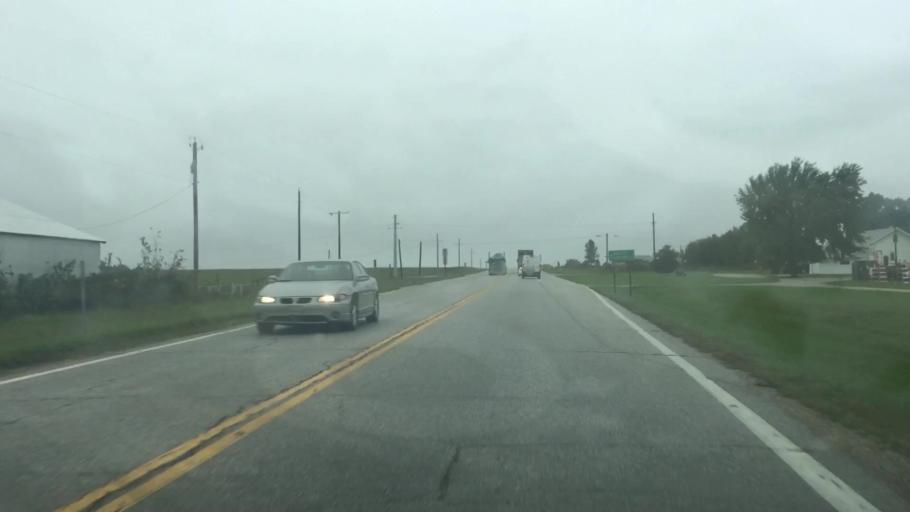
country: US
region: Kansas
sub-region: Anderson County
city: Garnett
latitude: 38.2284
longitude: -95.2483
